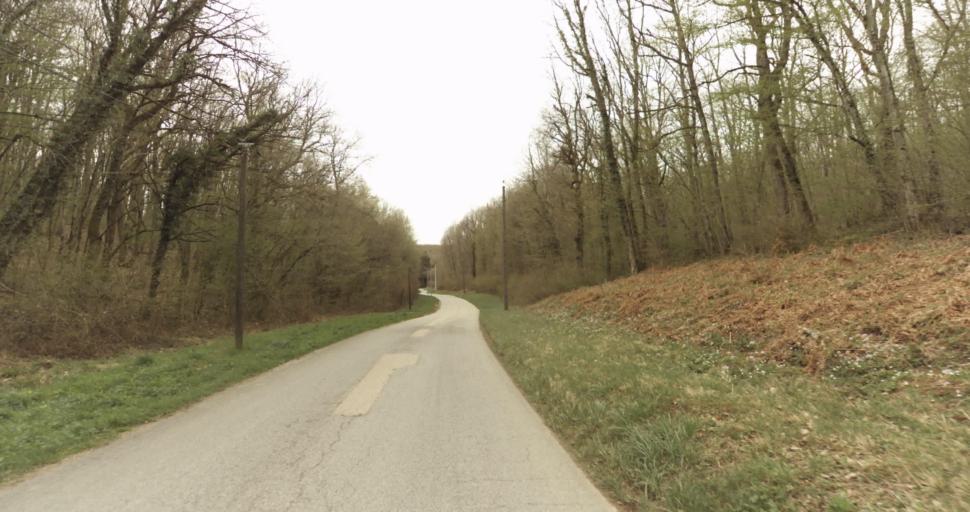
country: FR
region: Rhone-Alpes
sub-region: Departement de l'Ain
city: Ambronay
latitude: 45.9684
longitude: 5.3929
